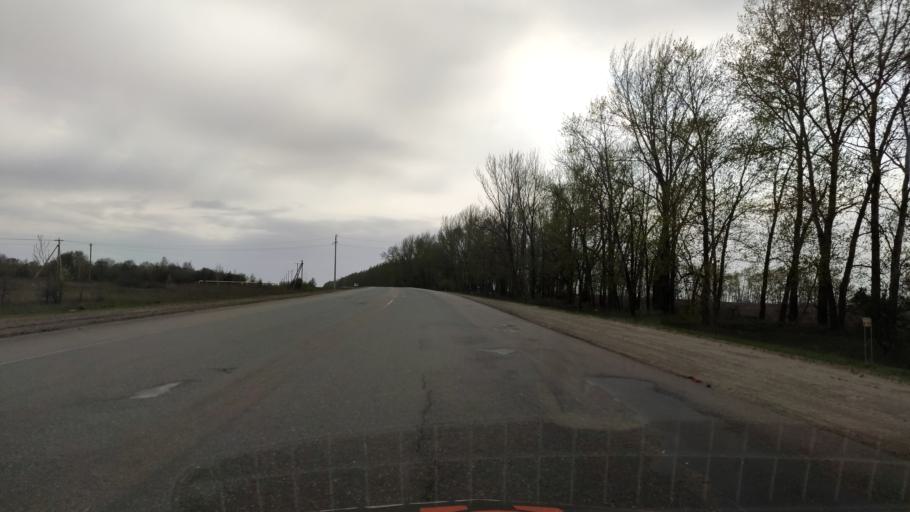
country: RU
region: Kursk
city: Gorshechnoye
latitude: 51.4641
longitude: 37.9274
